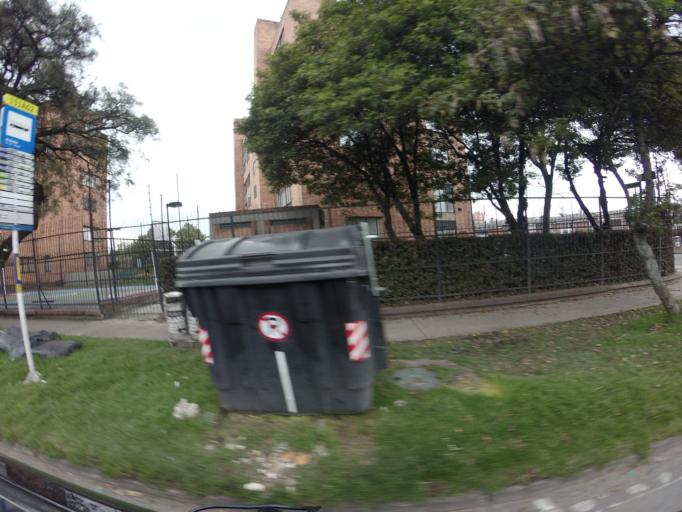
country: CO
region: Bogota D.C.
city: Barrio San Luis
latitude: 4.7097
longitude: -74.0660
